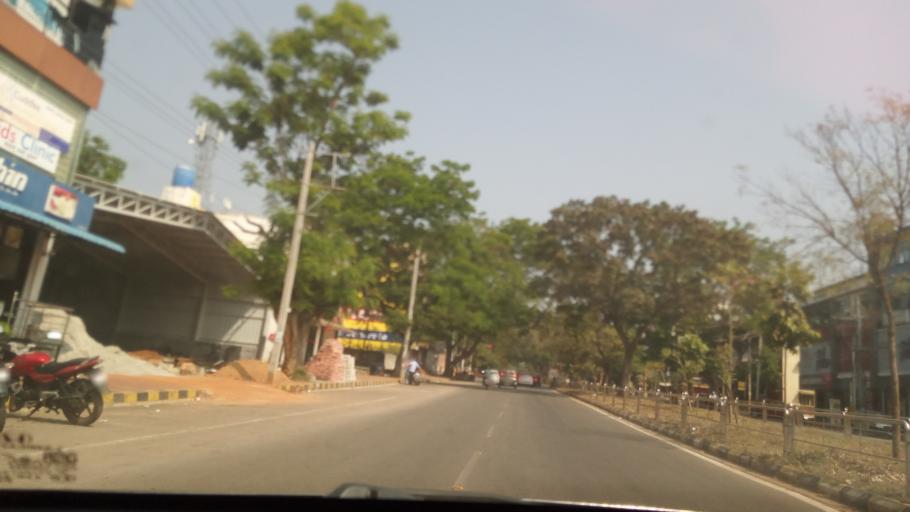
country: IN
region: Karnataka
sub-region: Mysore
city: Mysore
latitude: 12.3008
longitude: 76.6263
